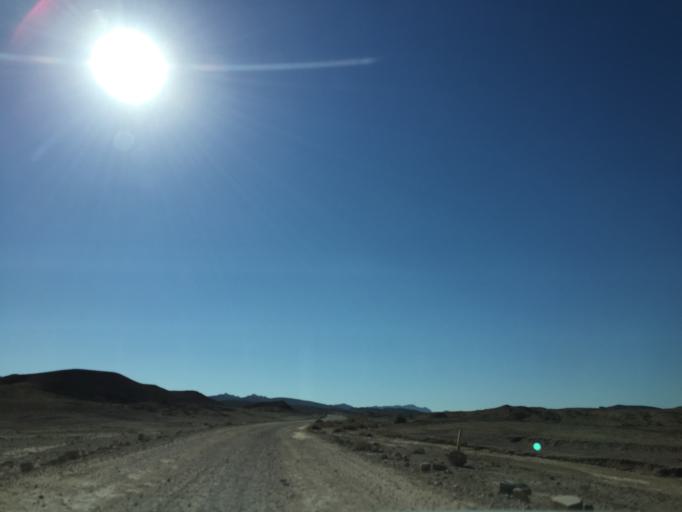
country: IL
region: Southern District
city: Mitzpe Ramon
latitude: 30.6153
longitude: 34.9134
